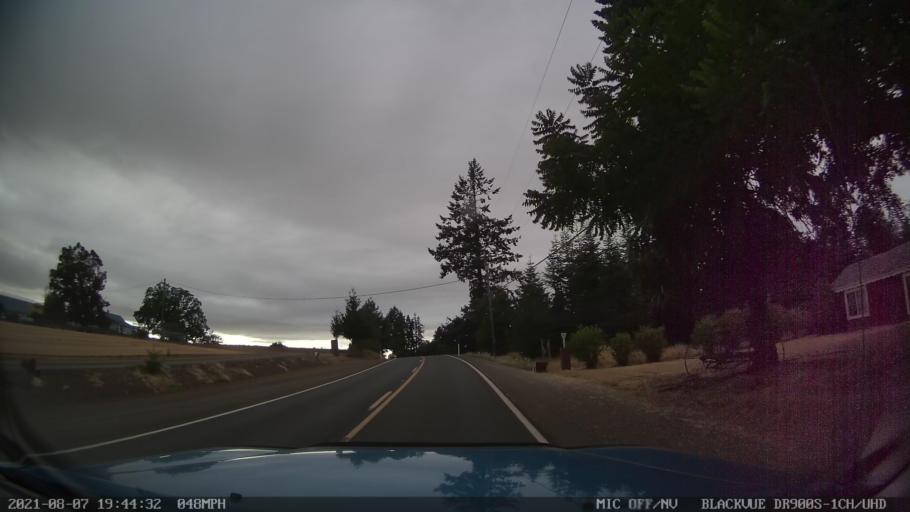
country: US
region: Oregon
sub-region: Marion County
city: Silverton
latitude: 44.9404
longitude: -122.6846
